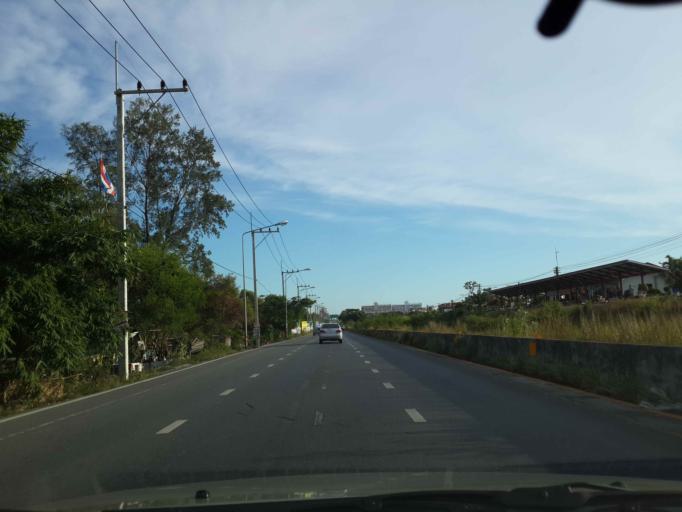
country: TH
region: Chon Buri
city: Phatthaya
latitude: 12.9410
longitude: 100.9102
